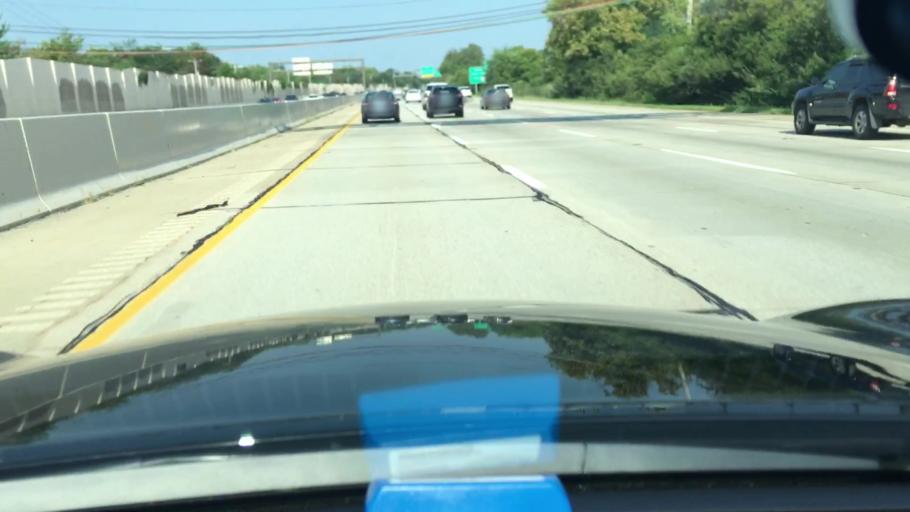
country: US
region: Pennsylvania
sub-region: Chester County
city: Chesterbrook
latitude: 40.0695
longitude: -75.4478
